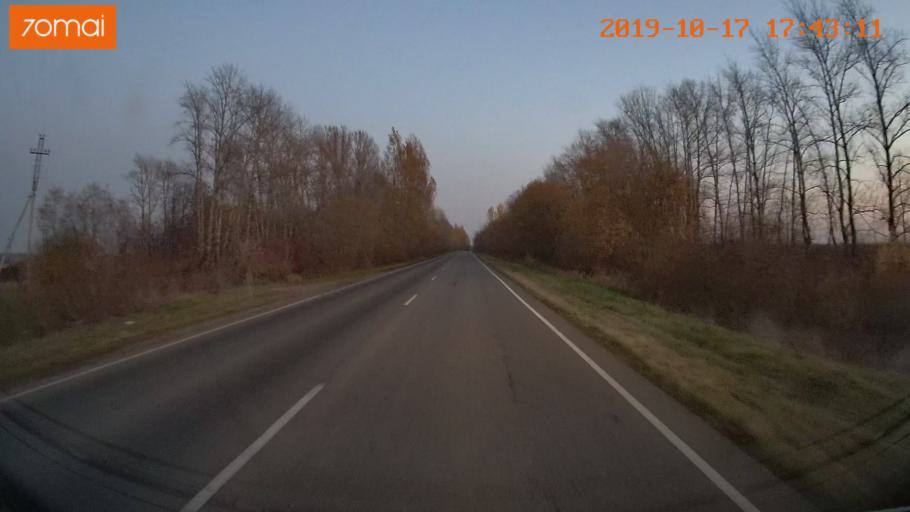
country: RU
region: Tula
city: Yepifan'
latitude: 53.7624
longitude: 38.6570
